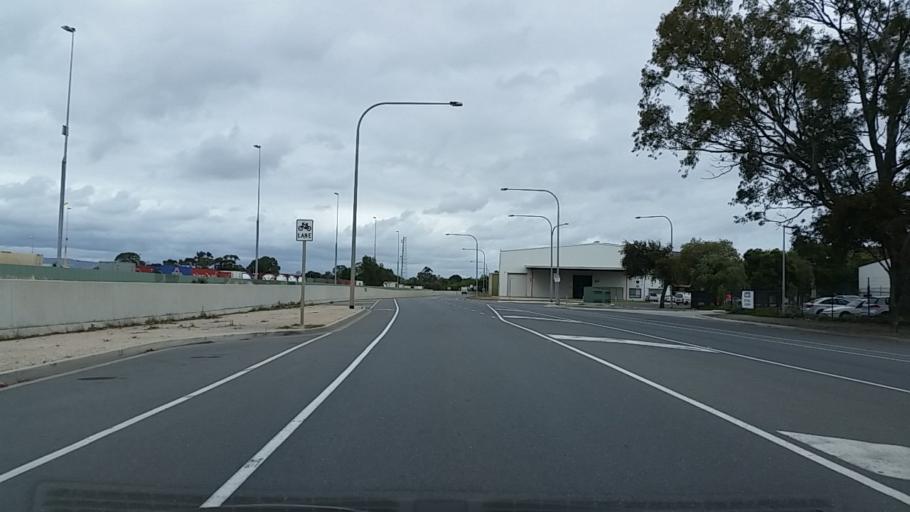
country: AU
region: South Australia
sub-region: Port Adelaide Enfield
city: Blair Athol
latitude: -34.8647
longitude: 138.5745
